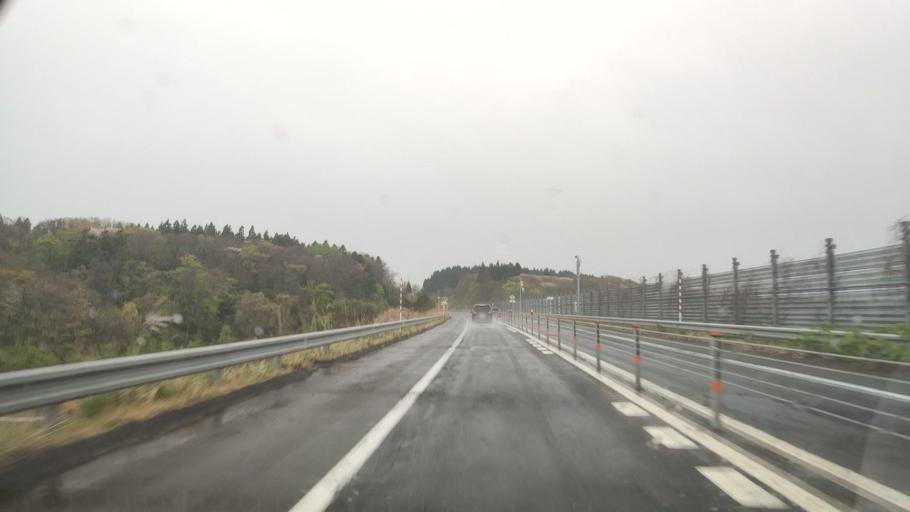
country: JP
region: Akita
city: Noshiromachi
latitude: 40.1767
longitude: 140.0576
